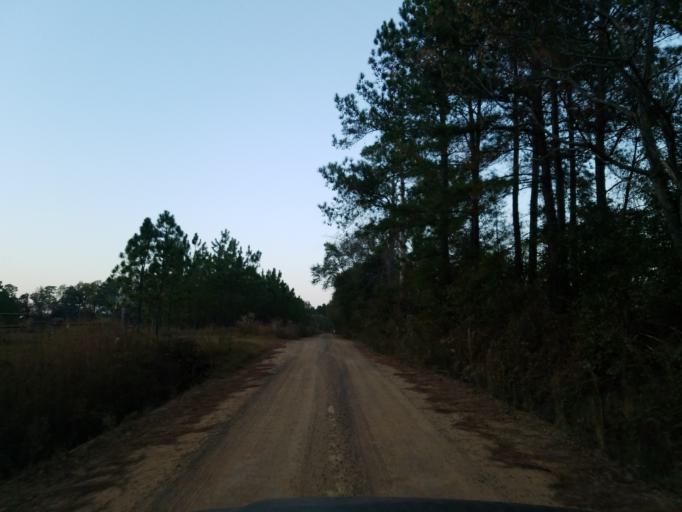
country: US
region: Georgia
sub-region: Turner County
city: Ashburn
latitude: 31.7316
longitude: -83.4837
